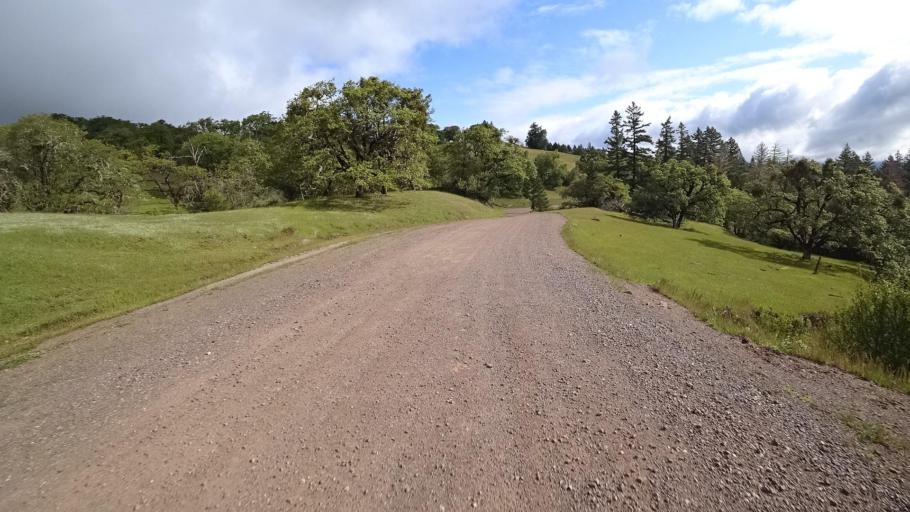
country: US
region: California
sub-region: Humboldt County
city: Redway
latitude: 40.2062
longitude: -123.6905
